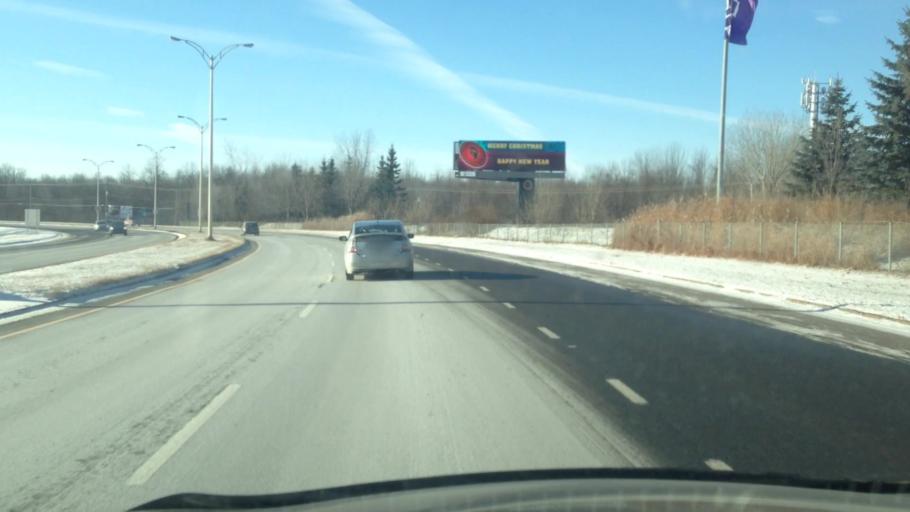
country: CA
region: Quebec
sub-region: Monteregie
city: Chateauguay
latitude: 45.3990
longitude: -73.6907
